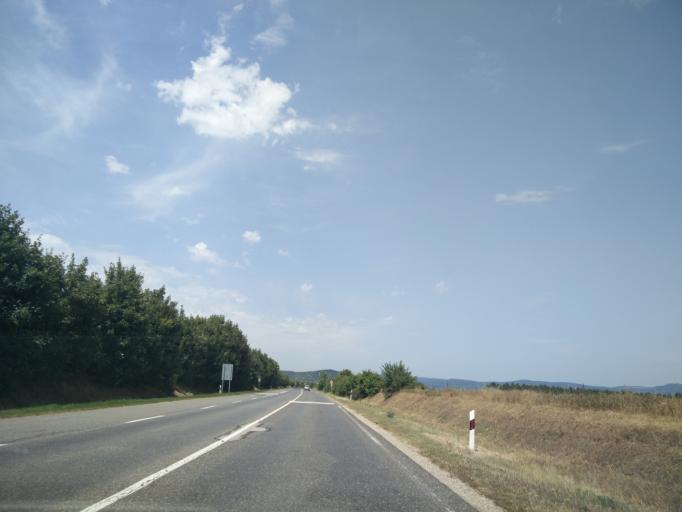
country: HU
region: Veszprem
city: Veszprem
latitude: 47.0851
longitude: 17.8854
